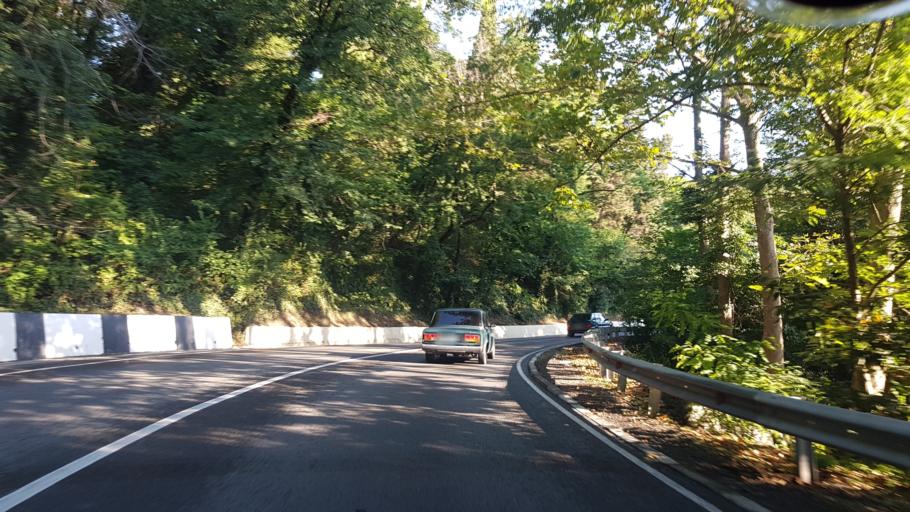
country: RU
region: Krasnodarskiy
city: Dagomys
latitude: 43.6610
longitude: 39.6376
